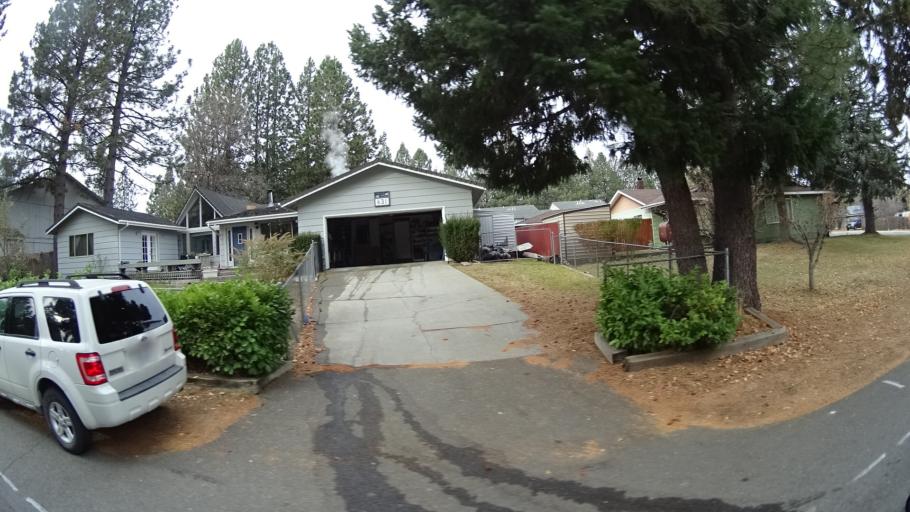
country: US
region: California
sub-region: Siskiyou County
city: Weed
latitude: 41.4138
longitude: -122.3858
